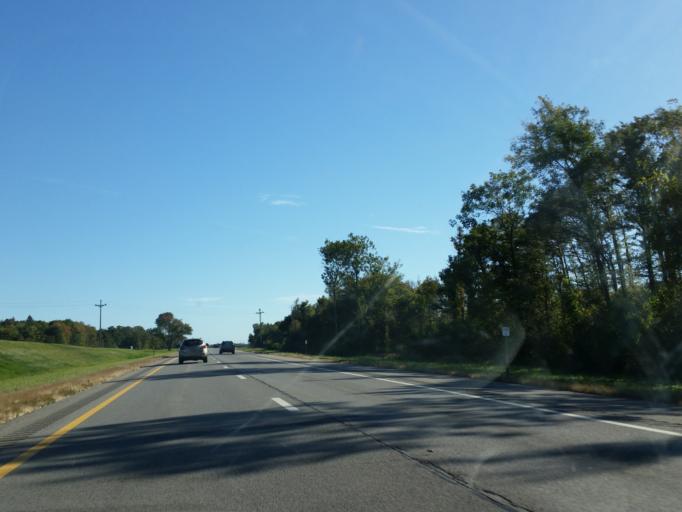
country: US
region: New York
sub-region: Erie County
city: Wanakah
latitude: 42.7284
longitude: -78.8748
